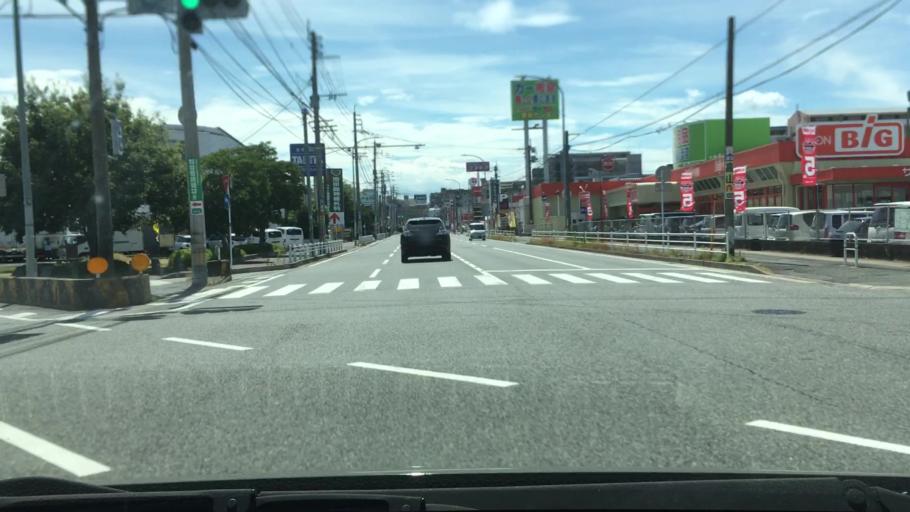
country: JP
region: Fukuoka
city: Onojo
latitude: 33.5528
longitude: 130.4561
